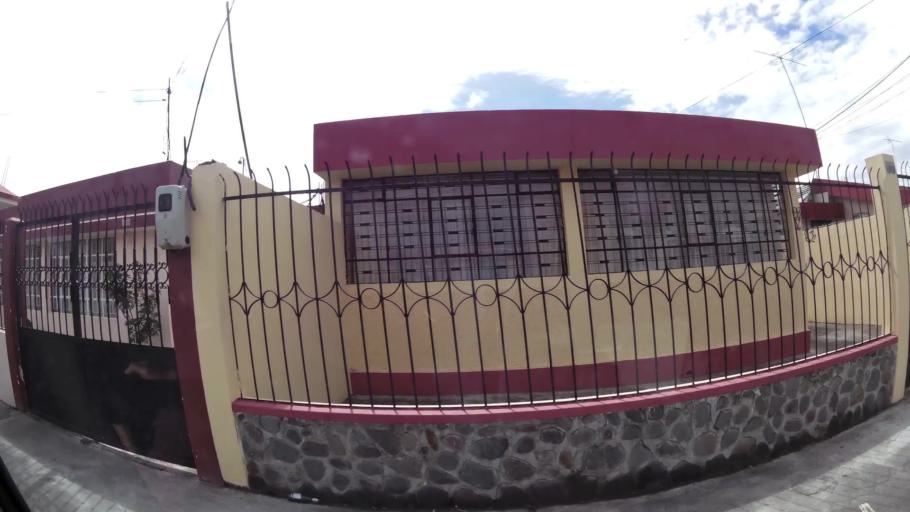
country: EC
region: Cotopaxi
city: Latacunga
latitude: -0.9268
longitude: -78.6090
